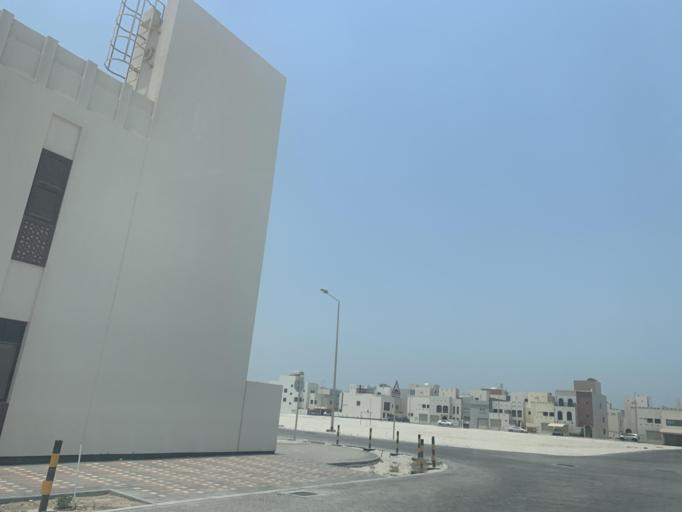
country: BH
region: Muharraq
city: Al Hadd
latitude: 26.2333
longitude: 50.6781
